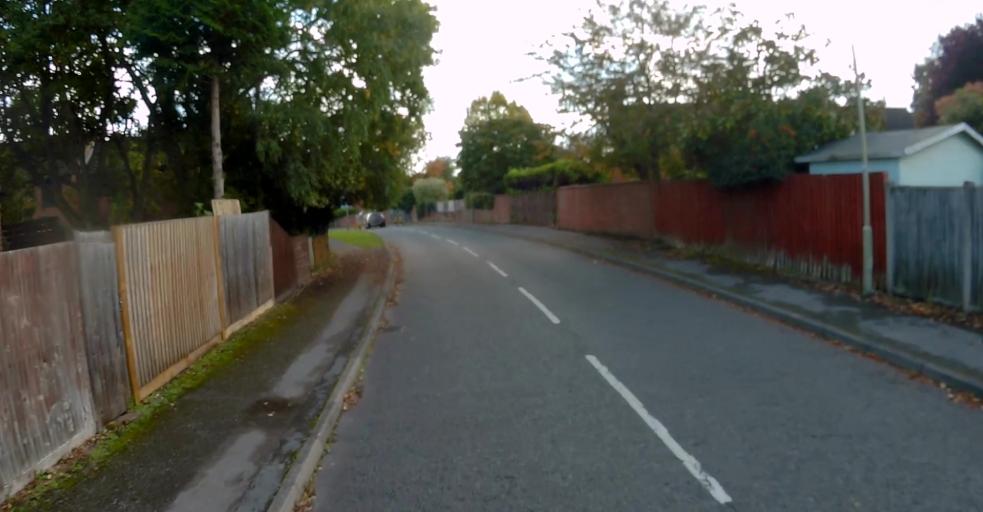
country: GB
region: England
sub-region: Hampshire
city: Fleet
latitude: 51.2955
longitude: -0.8277
